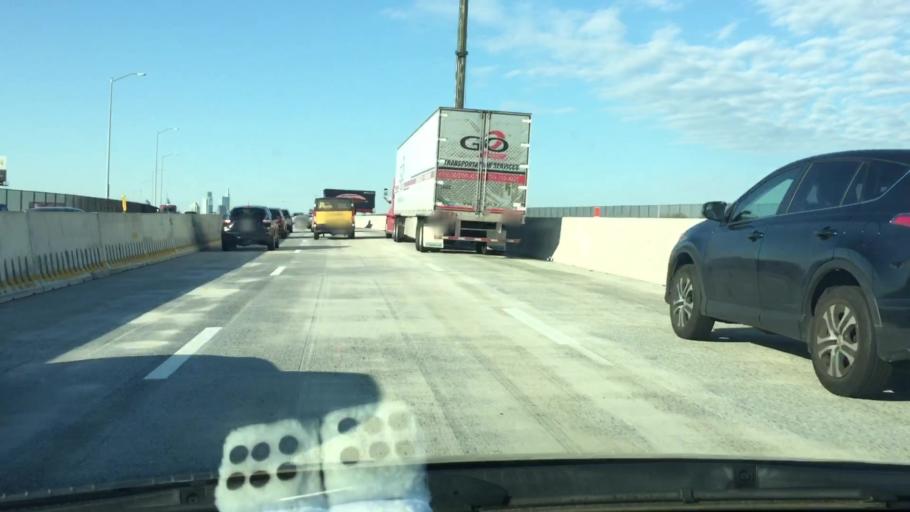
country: US
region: New Jersey
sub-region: Camden County
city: Merchantville
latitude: 39.9792
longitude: -75.1080
